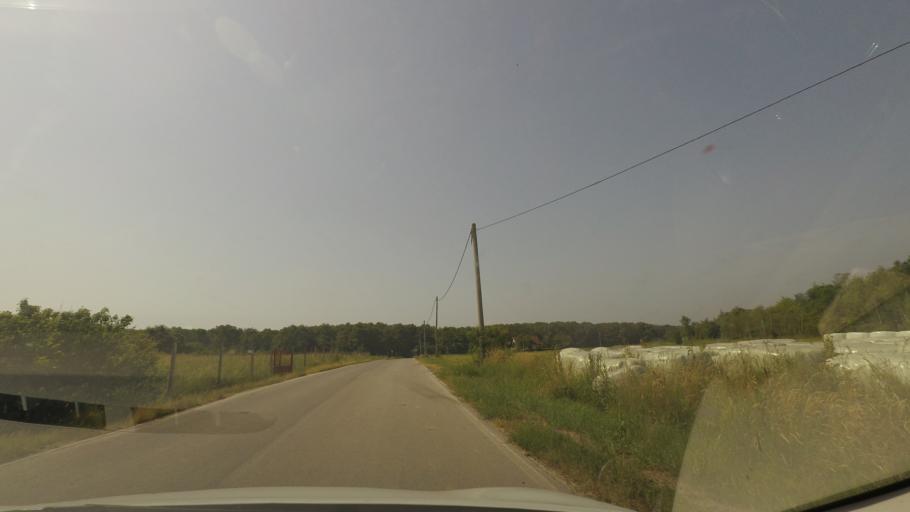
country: HR
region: Karlovacka
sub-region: Grad Karlovac
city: Karlovac
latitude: 45.4839
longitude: 15.5899
